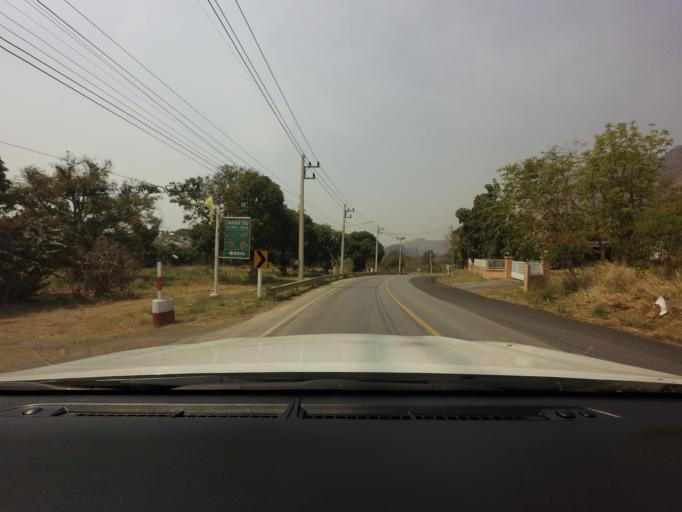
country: TH
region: Sara Buri
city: Muak Lek
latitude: 14.5789
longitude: 101.2614
